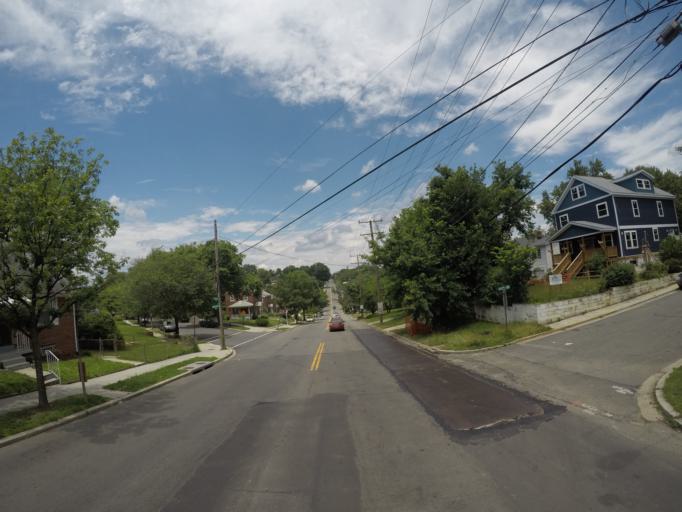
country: US
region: Maryland
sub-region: Montgomery County
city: Takoma Park
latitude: 38.9672
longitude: -77.0044
